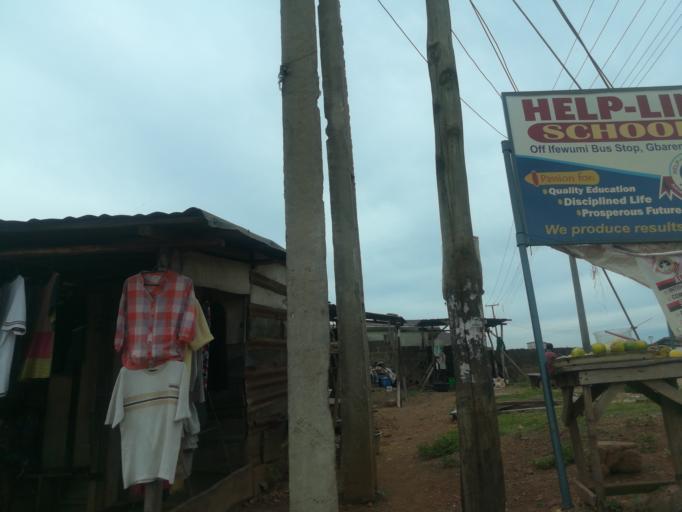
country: NG
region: Oyo
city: Ibadan
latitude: 7.3764
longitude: 3.9533
